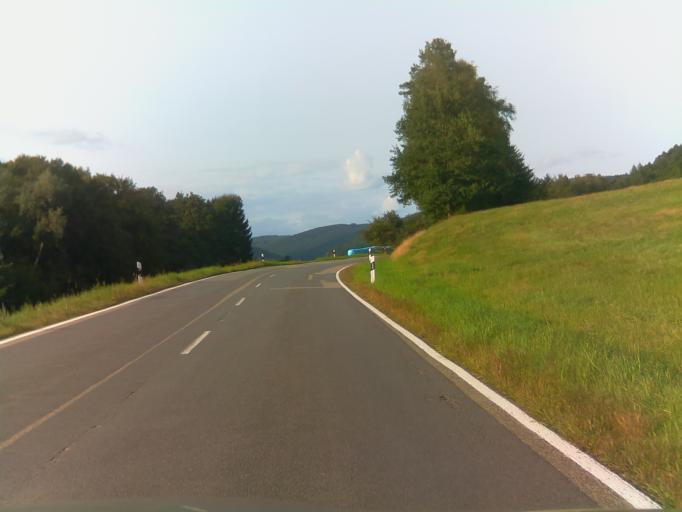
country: DE
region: Baden-Wuerttemberg
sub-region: Karlsruhe Region
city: Heddesbach
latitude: 49.5101
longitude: 8.8537
